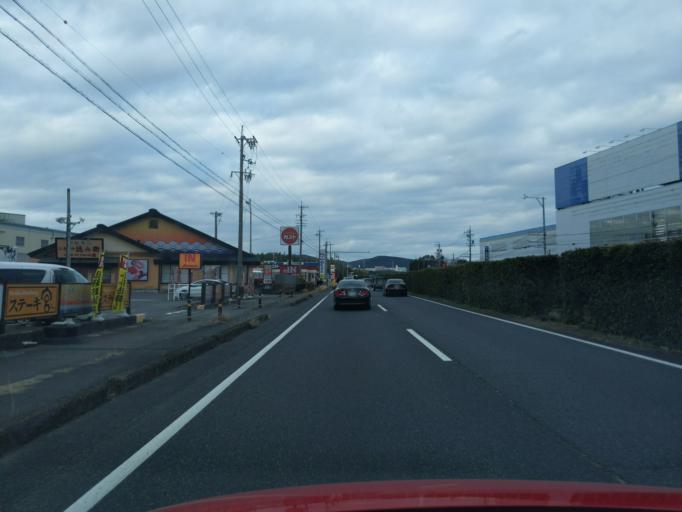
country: JP
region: Aichi
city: Kasugai
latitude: 35.2878
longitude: 137.0184
